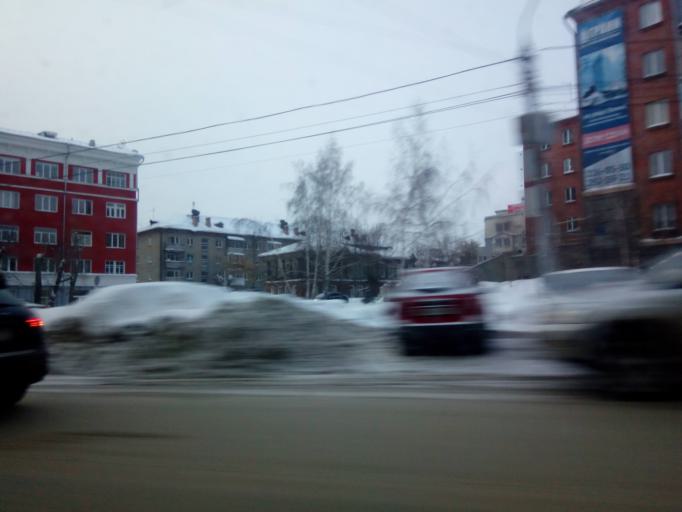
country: RU
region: Novosibirsk
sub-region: Novosibirskiy Rayon
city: Novosibirsk
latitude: 55.0308
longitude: 82.9090
